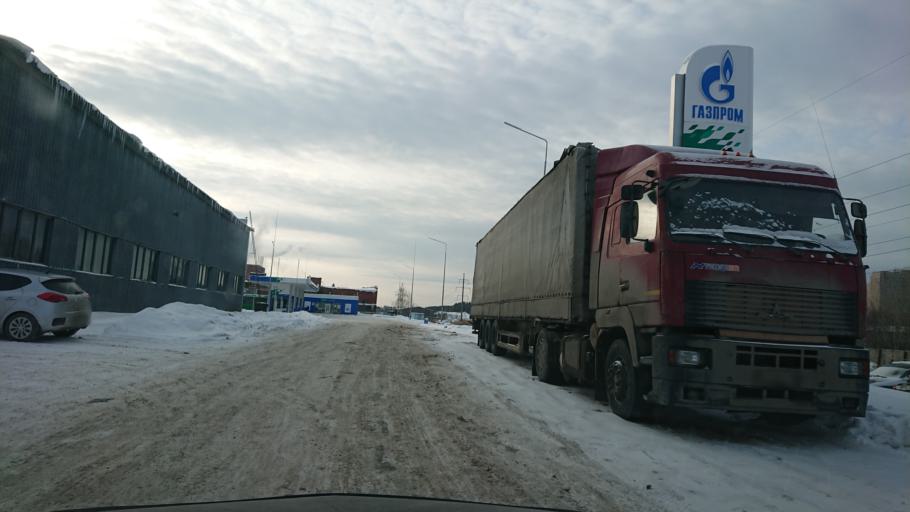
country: RU
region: Sverdlovsk
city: Sovkhoznyy
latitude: 56.7783
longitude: 60.5615
